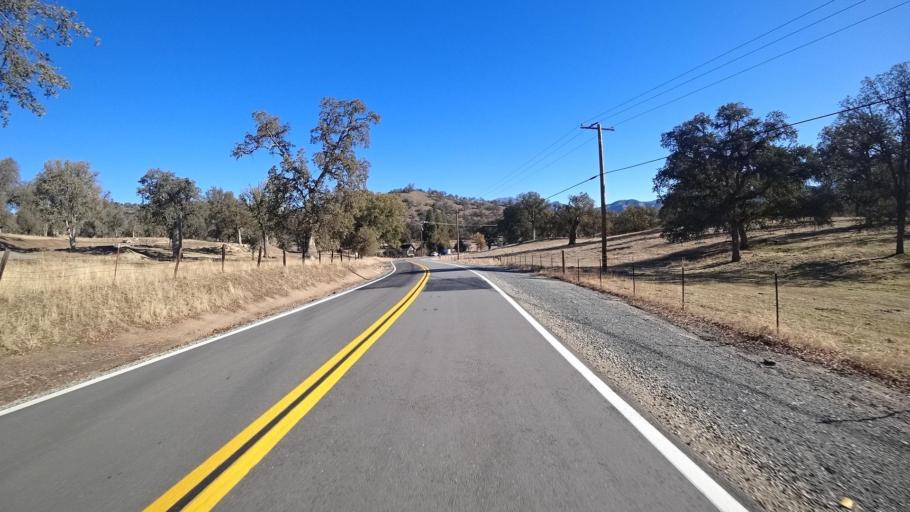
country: US
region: California
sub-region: Kern County
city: Alta Sierra
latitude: 35.7104
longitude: -118.7419
